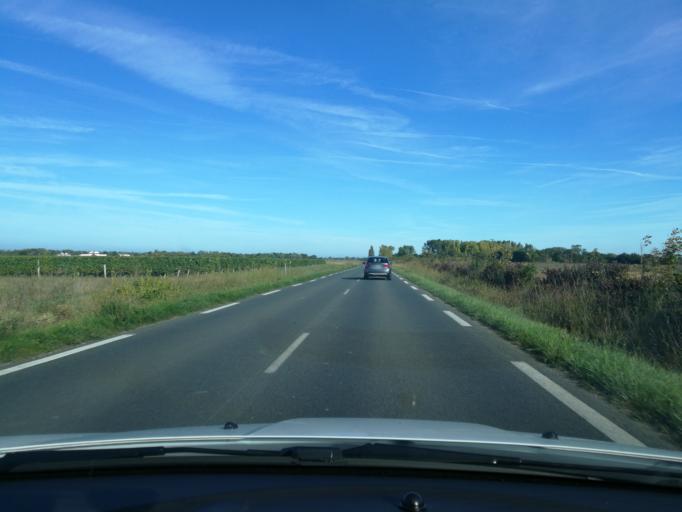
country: FR
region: Poitou-Charentes
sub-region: Departement de la Charente-Maritime
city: Saint-Denis-d'Oleron
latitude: 45.9885
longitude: -1.3599
